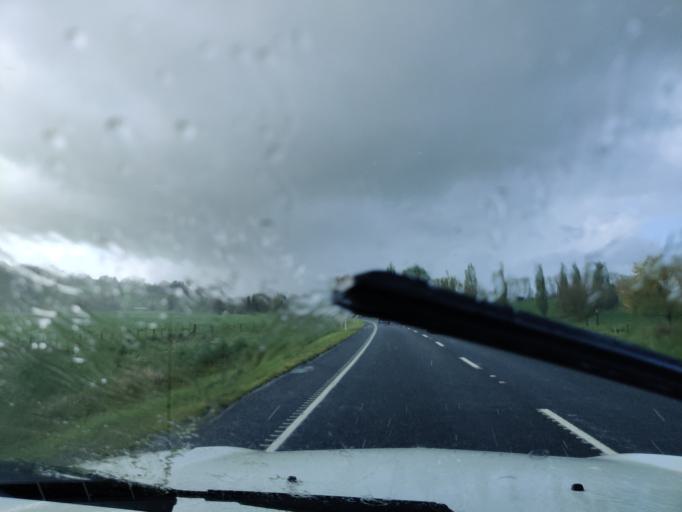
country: NZ
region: Waikato
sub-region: Matamata-Piako District
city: Matamata
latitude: -37.9751
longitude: 175.6956
